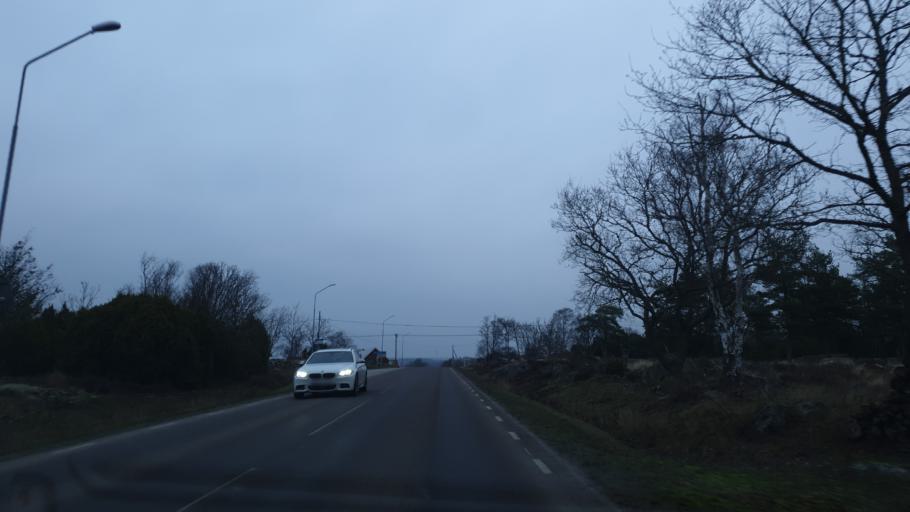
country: SE
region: Blekinge
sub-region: Karlskrona Kommun
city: Sturko
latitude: 56.1303
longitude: 15.7388
